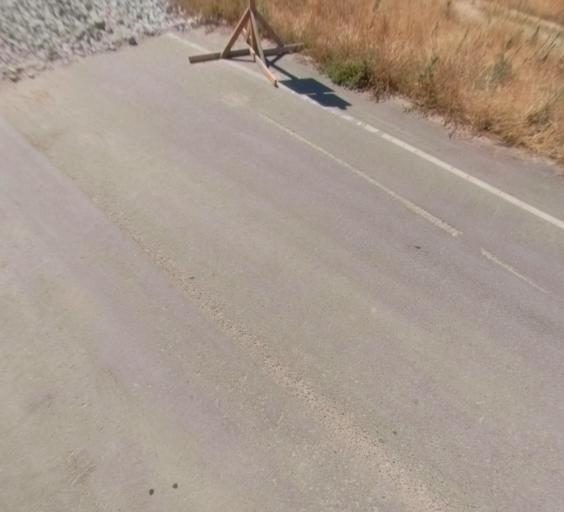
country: US
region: California
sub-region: Madera County
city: Parksdale
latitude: 36.9671
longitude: -120.0181
